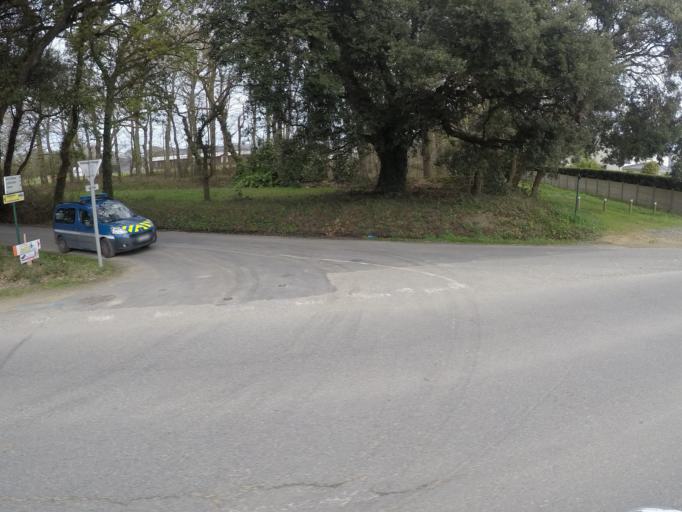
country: FR
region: Brittany
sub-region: Departement des Cotes-d'Armor
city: Plouha
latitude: 48.6892
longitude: -2.9317
